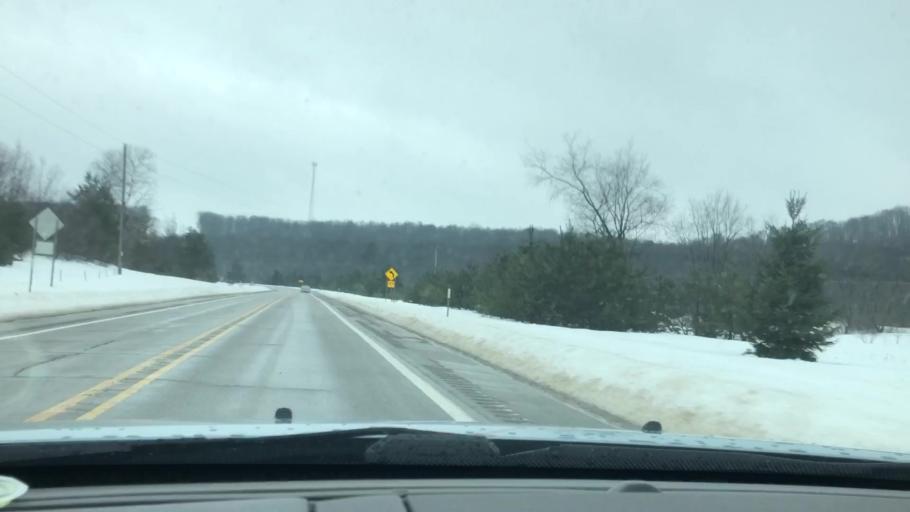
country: US
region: Michigan
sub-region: Charlevoix County
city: Boyne City
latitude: 45.0836
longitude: -84.9236
